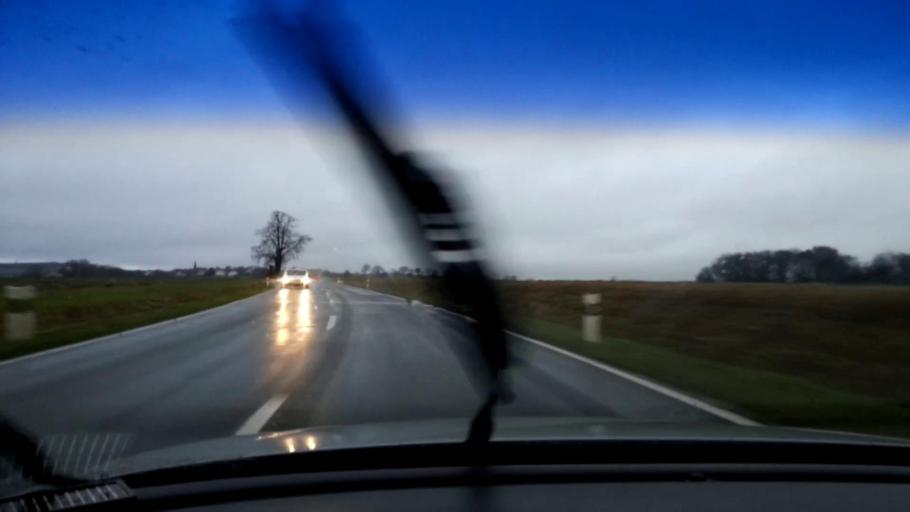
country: DE
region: Bavaria
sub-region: Upper Franconia
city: Schesslitz
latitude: 49.9912
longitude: 11.0080
